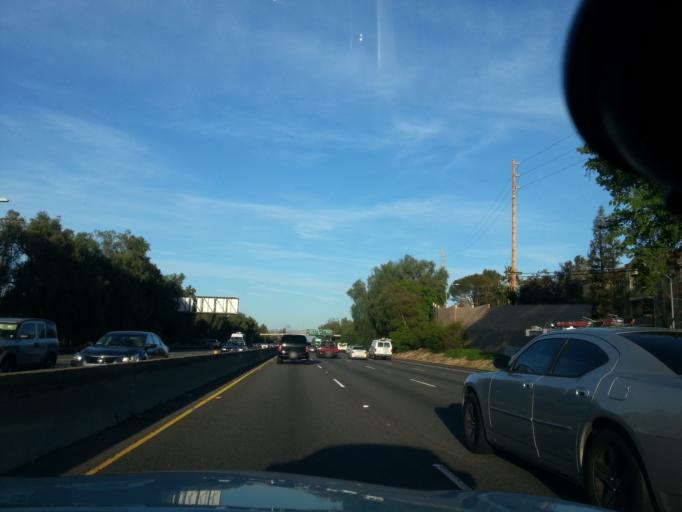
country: US
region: California
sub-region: Los Angeles County
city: Calabasas
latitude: 34.1623
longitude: -118.6296
